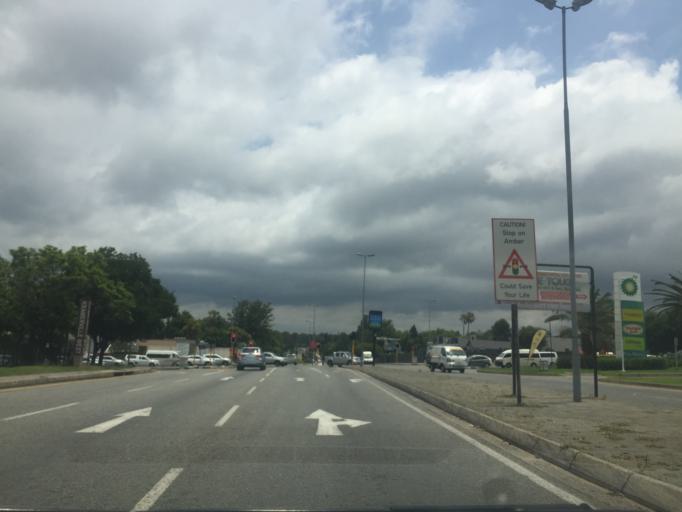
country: ZA
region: Gauteng
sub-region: City of Johannesburg Metropolitan Municipality
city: Modderfontein
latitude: -26.0884
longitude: 28.0794
